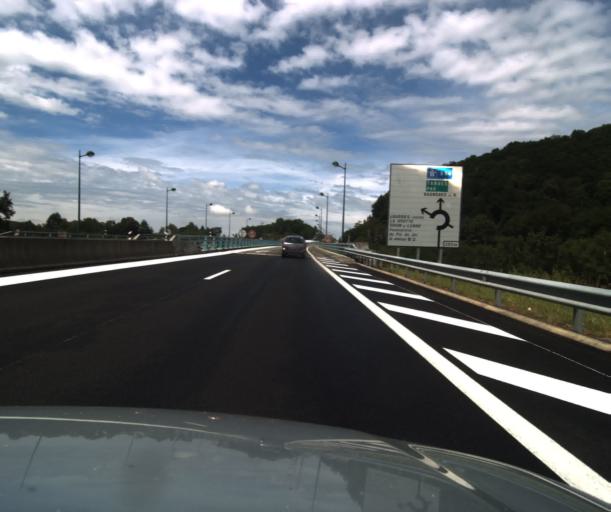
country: FR
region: Midi-Pyrenees
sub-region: Departement des Hautes-Pyrenees
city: Lourdes
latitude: 43.0802
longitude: -0.0446
